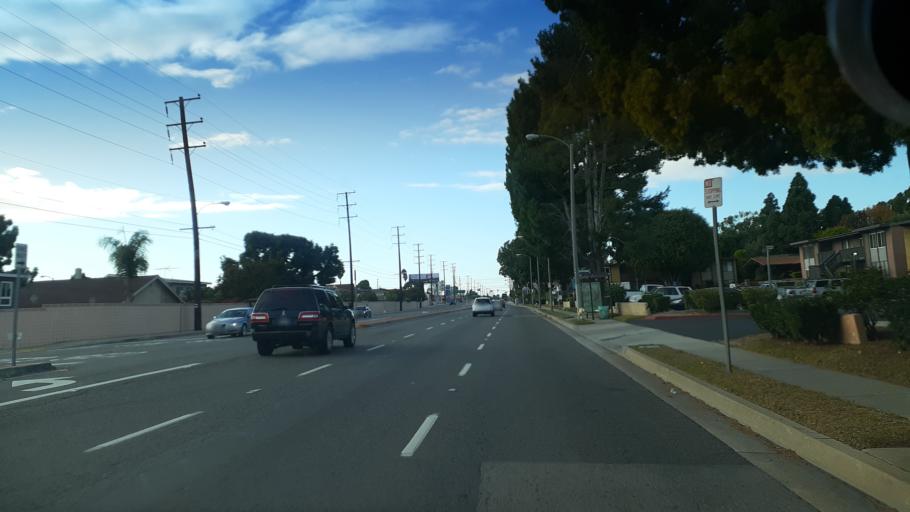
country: US
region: California
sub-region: Los Angeles County
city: West Carson
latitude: 33.8116
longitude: -118.2934
